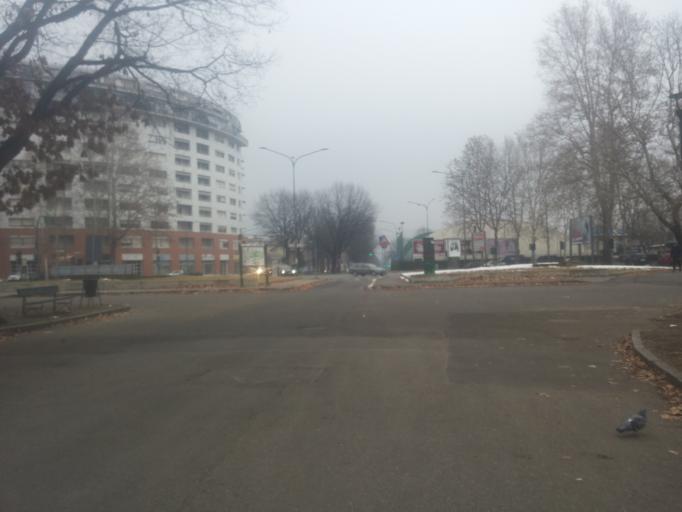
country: IT
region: Piedmont
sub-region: Provincia di Torino
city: Lesna
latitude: 45.0581
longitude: 7.6340
